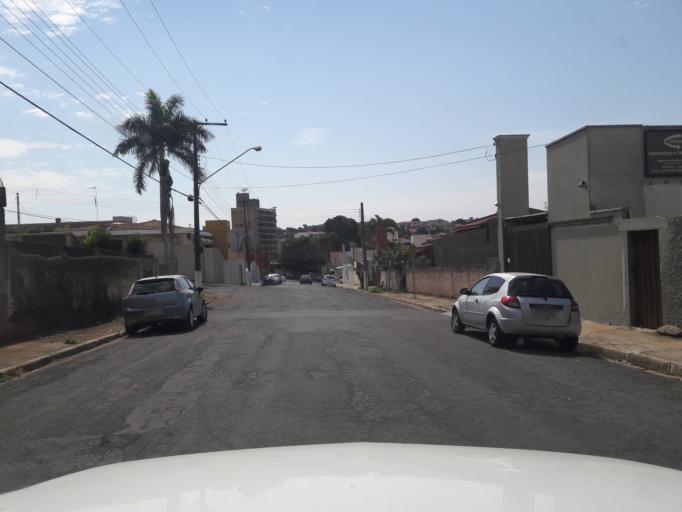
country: BR
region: Sao Paulo
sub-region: Moji-Guacu
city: Mogi-Gaucu
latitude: -22.3681
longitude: -46.9441
